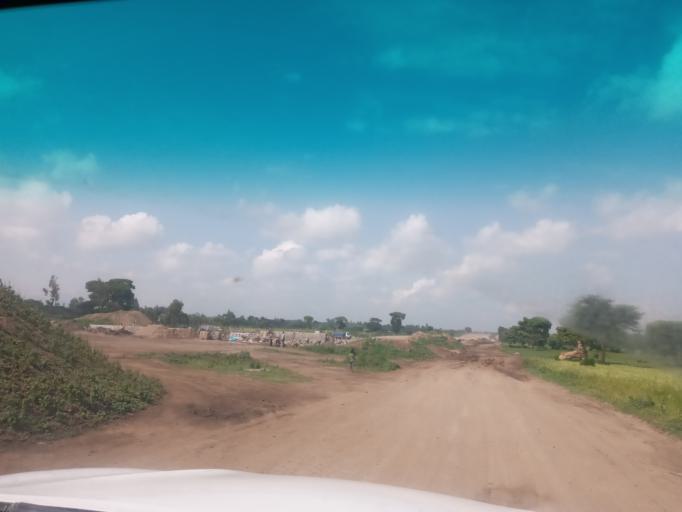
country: ET
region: Oromiya
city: Shashemene
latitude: 7.2850
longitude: 38.6080
